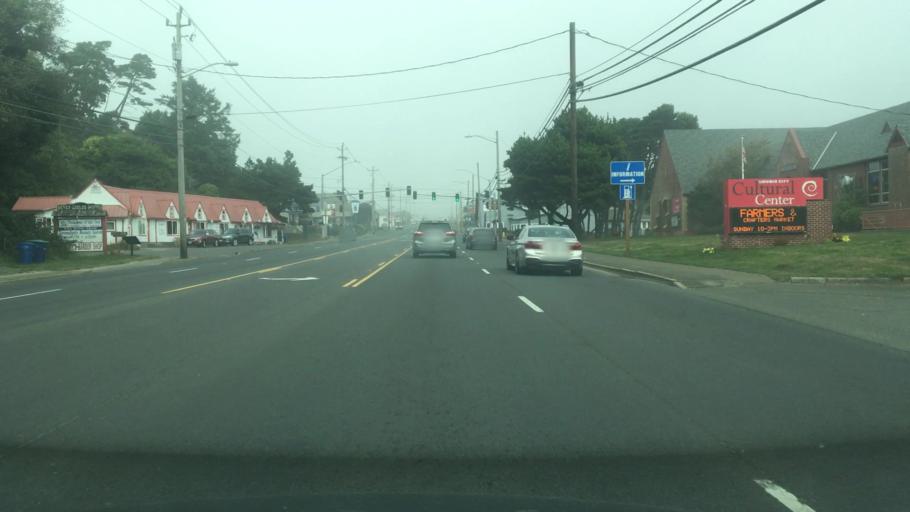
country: US
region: Oregon
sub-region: Lincoln County
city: Lincoln City
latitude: 44.9698
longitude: -124.0150
